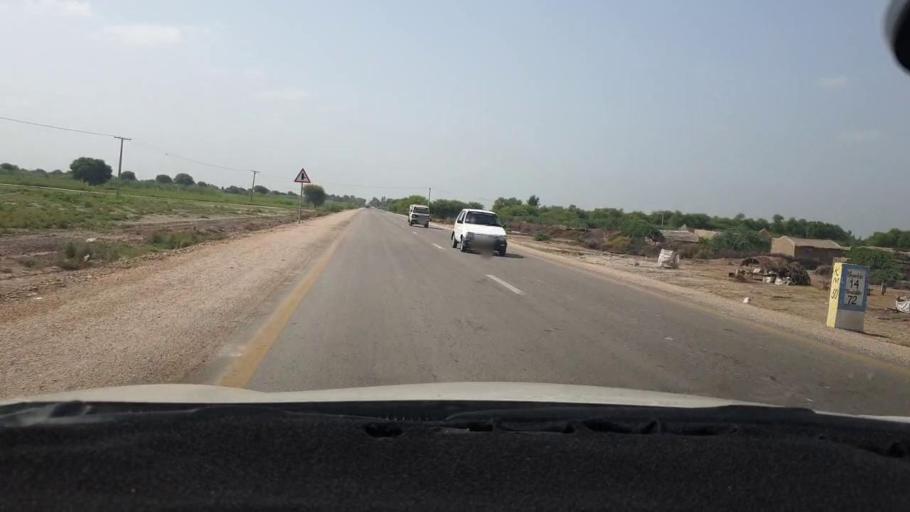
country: PK
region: Sindh
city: Mirpur Khas
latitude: 25.6490
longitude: 69.0980
